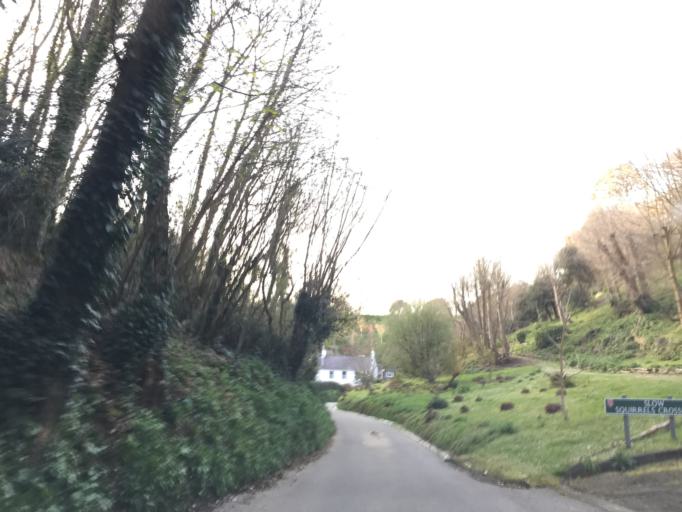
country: JE
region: St Helier
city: Saint Helier
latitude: 49.2320
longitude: -2.0496
